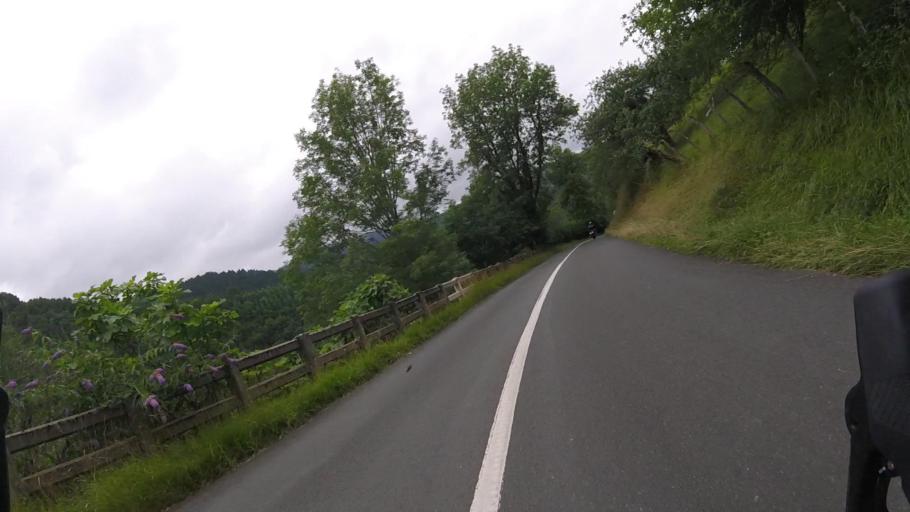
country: ES
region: Basque Country
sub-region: Provincia de Guipuzcoa
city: Irun
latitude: 43.2711
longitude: -1.8064
